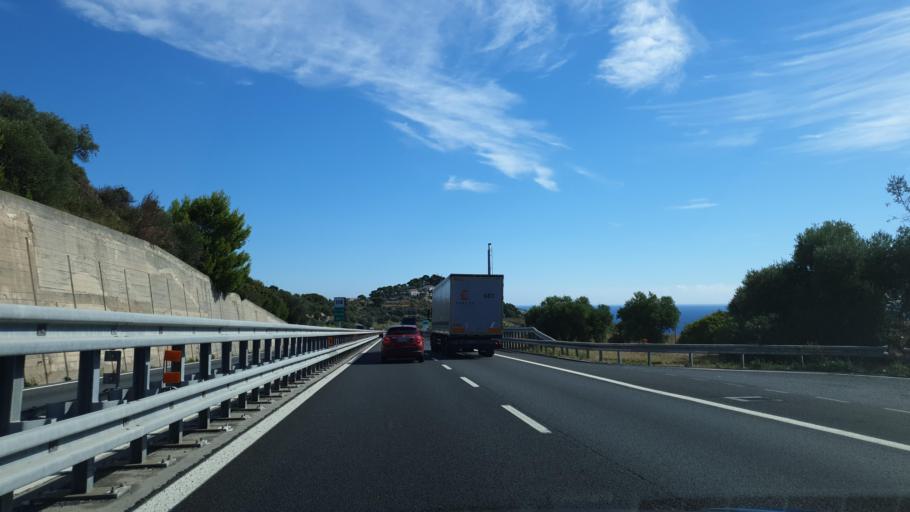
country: IT
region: Liguria
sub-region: Provincia di Imperia
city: Costarainera
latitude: 43.8506
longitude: 7.9377
